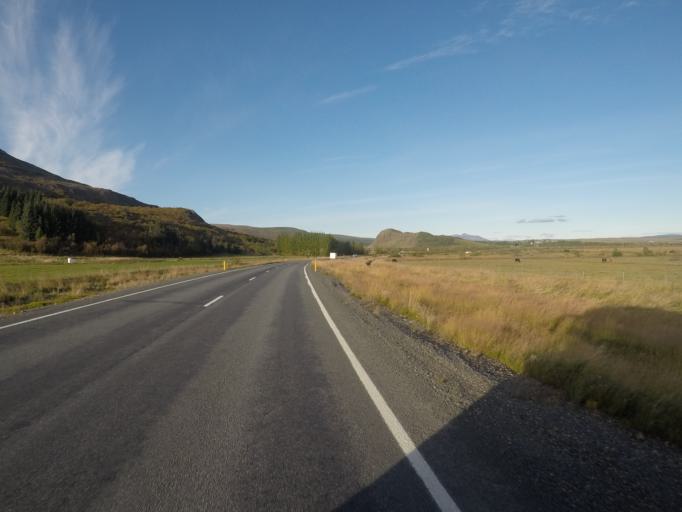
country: IS
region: South
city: Selfoss
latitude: 64.3017
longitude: -20.3300
